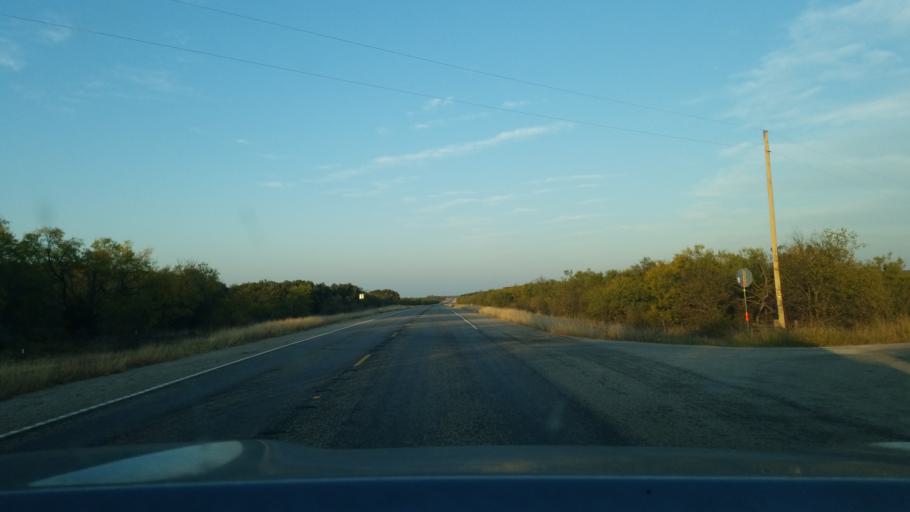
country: US
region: Texas
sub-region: Eastland County
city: Cisco
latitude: 32.4418
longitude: -98.9159
